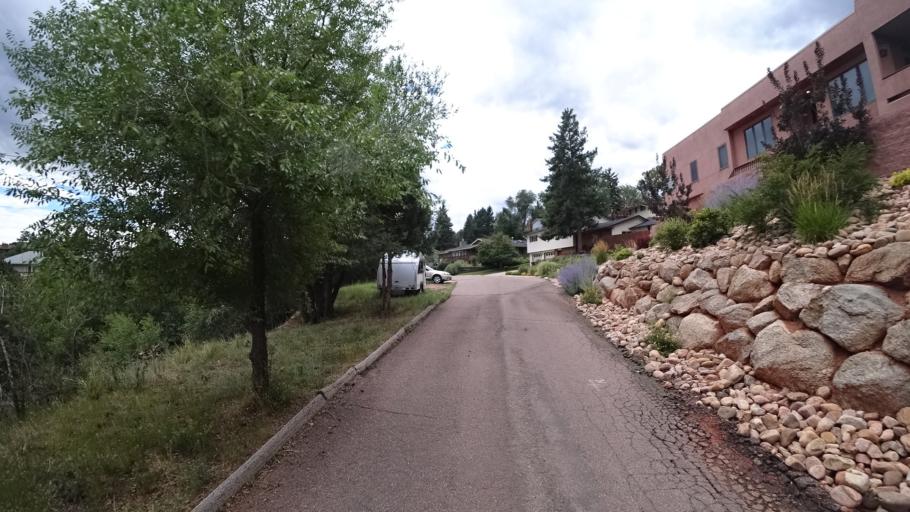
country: US
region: Colorado
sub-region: El Paso County
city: Manitou Springs
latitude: 38.8524
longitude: -104.8921
